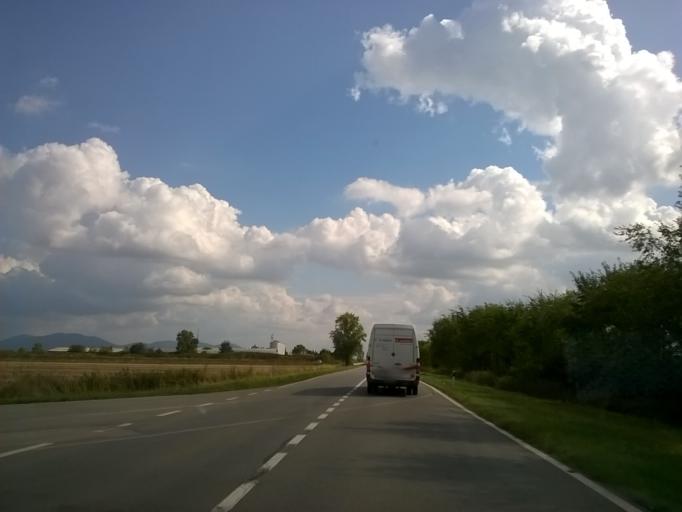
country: RS
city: Margita
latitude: 45.1864
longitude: 21.2030
